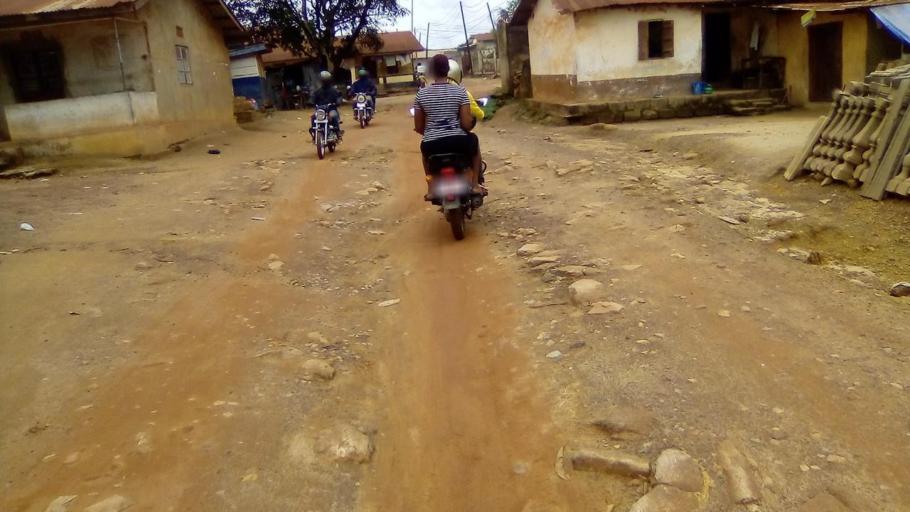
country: SL
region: Southern Province
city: Bo
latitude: 7.9450
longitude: -11.7393
